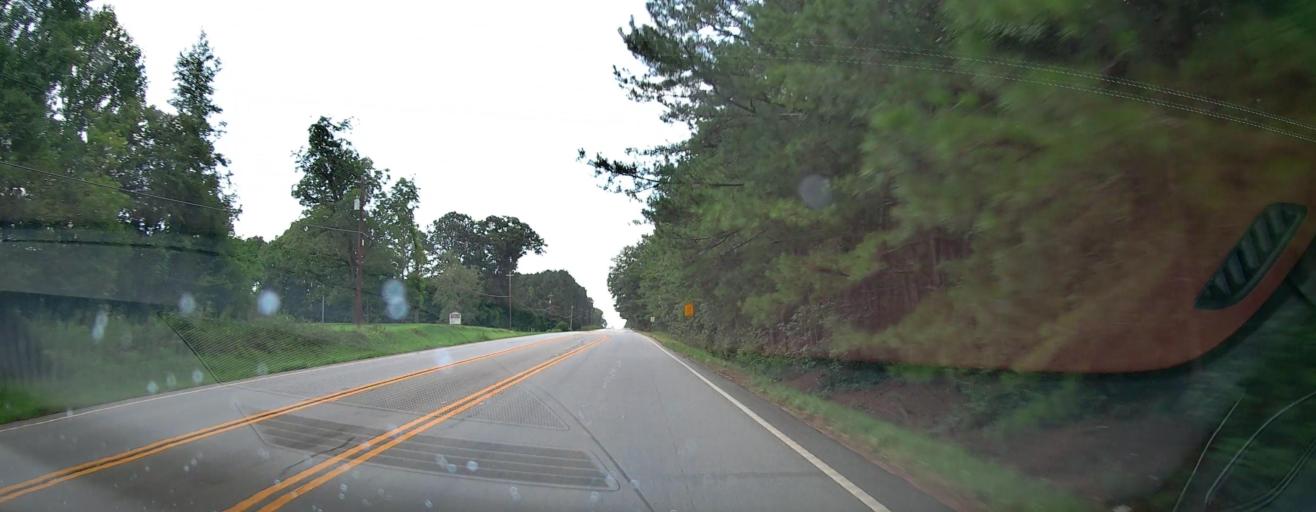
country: US
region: Georgia
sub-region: Coweta County
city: Senoia
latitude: 33.1860
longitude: -84.5803
